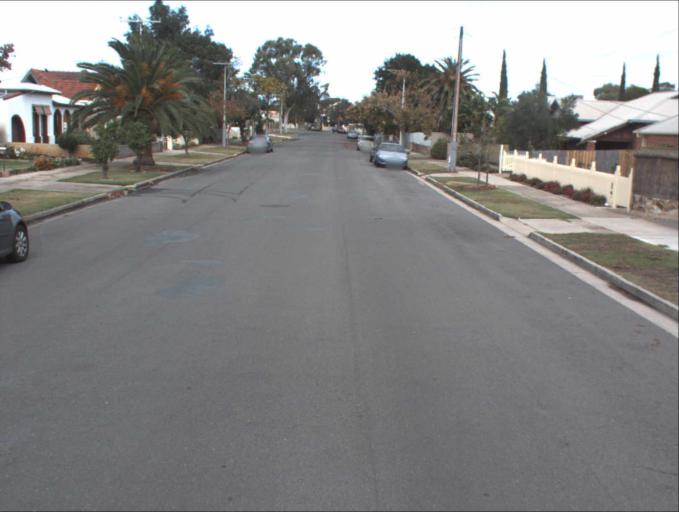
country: AU
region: South Australia
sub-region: Charles Sturt
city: West Lakes Shore
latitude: -34.8450
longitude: 138.4831
